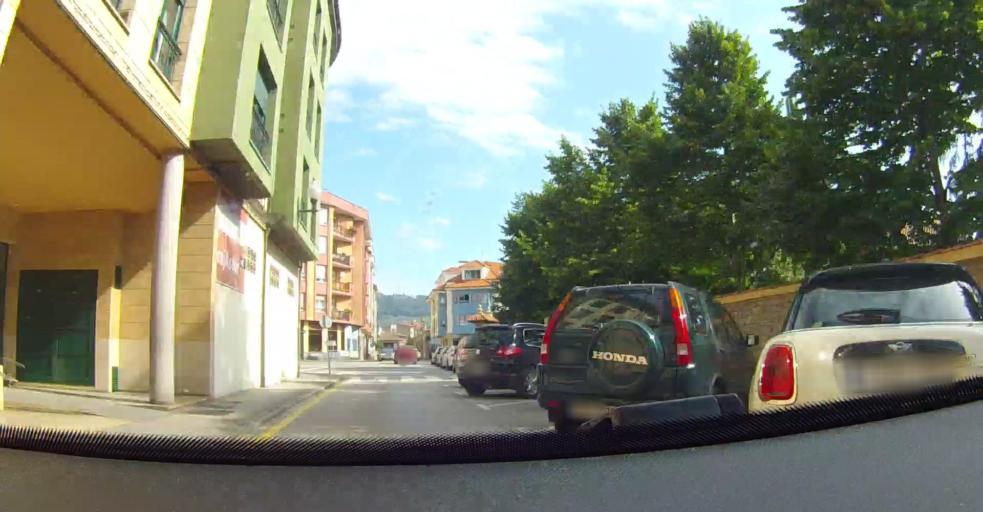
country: ES
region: Asturias
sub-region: Province of Asturias
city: Villaviciosa
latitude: 43.4798
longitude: -5.4370
